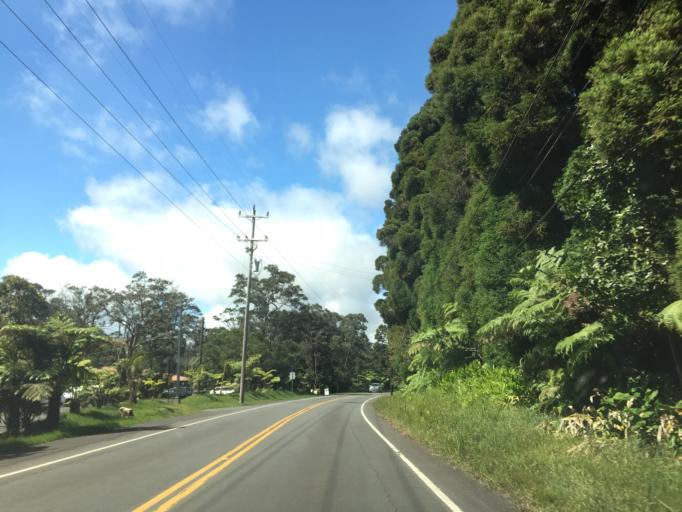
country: US
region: Hawaii
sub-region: Hawaii County
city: Volcano
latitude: 19.4248
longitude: -155.2395
